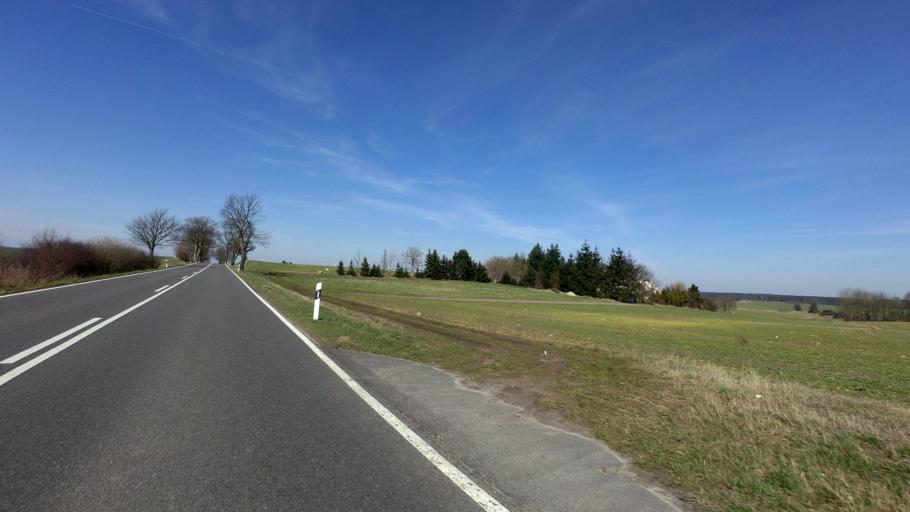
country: DE
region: Brandenburg
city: Protzel
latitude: 52.6146
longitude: 14.0200
